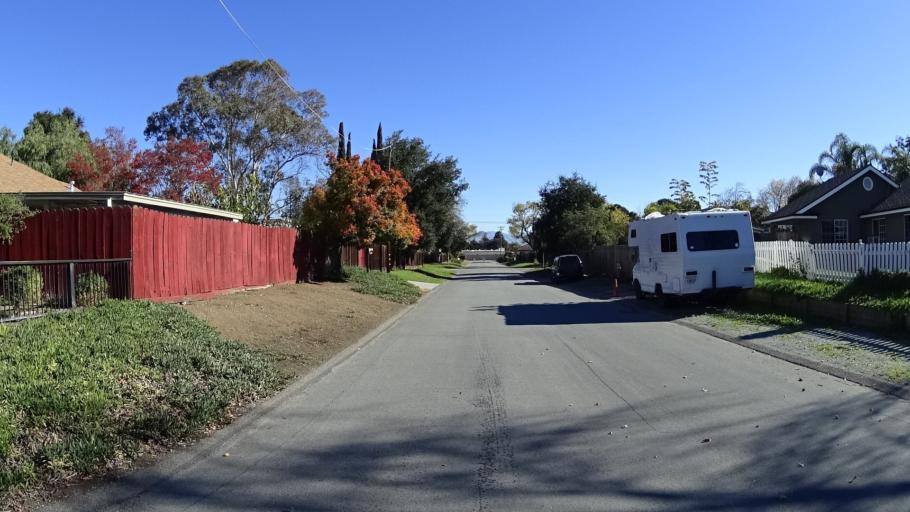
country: US
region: California
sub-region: Santa Clara County
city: Sunnyvale
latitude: 37.3483
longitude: -122.0120
